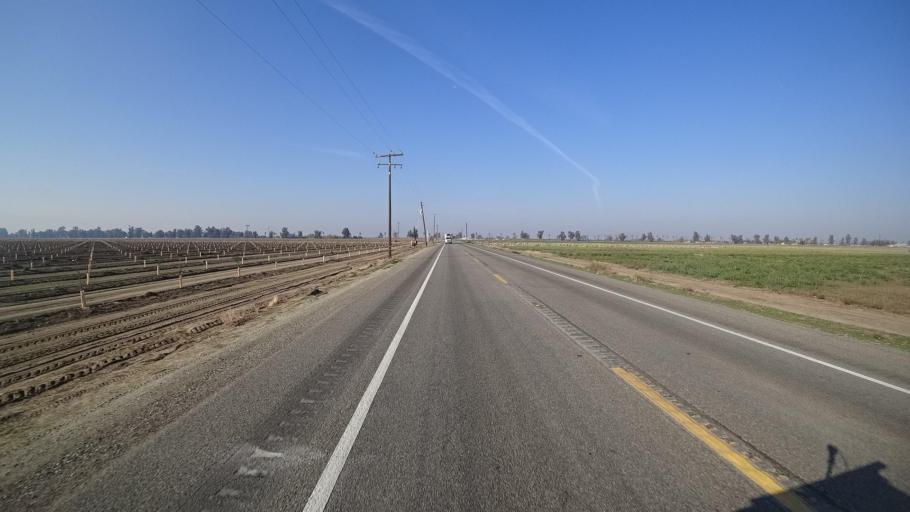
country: US
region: California
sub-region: Kern County
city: Greenfield
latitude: 35.2086
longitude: -118.9922
